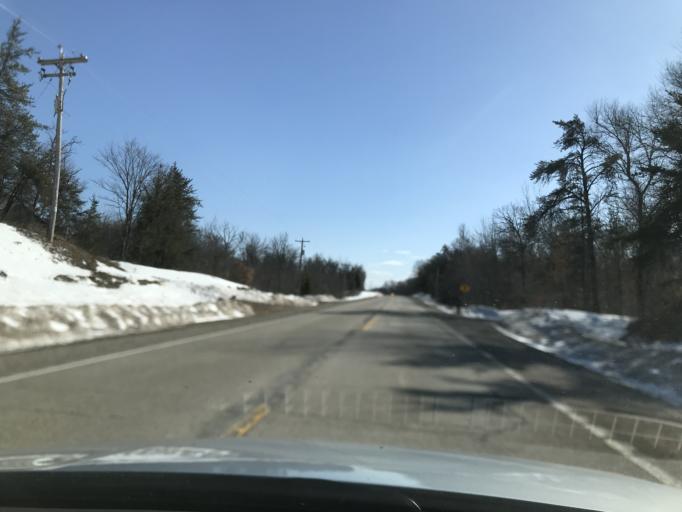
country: US
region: Wisconsin
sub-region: Marinette County
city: Niagara
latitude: 45.3446
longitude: -88.1015
